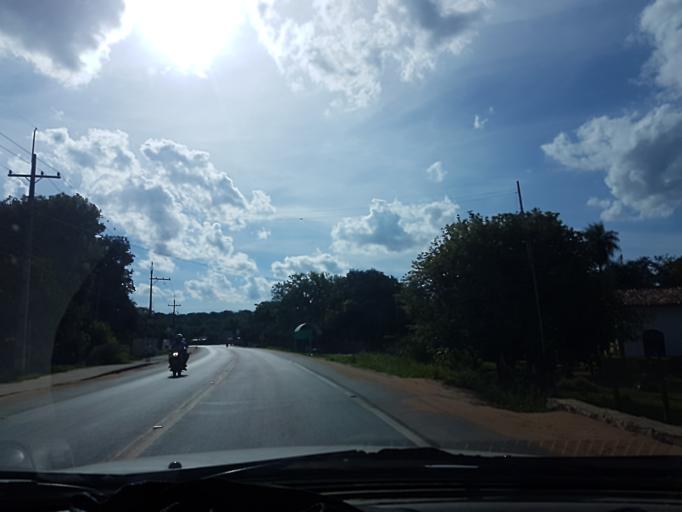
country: PY
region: Central
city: Limpio
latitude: -25.2356
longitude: -57.4482
